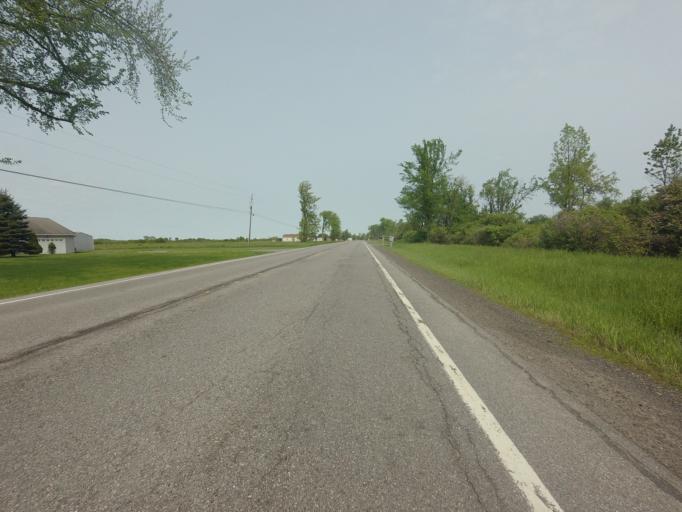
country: US
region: New York
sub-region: Jefferson County
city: Dexter
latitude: 44.0243
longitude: -76.0376
